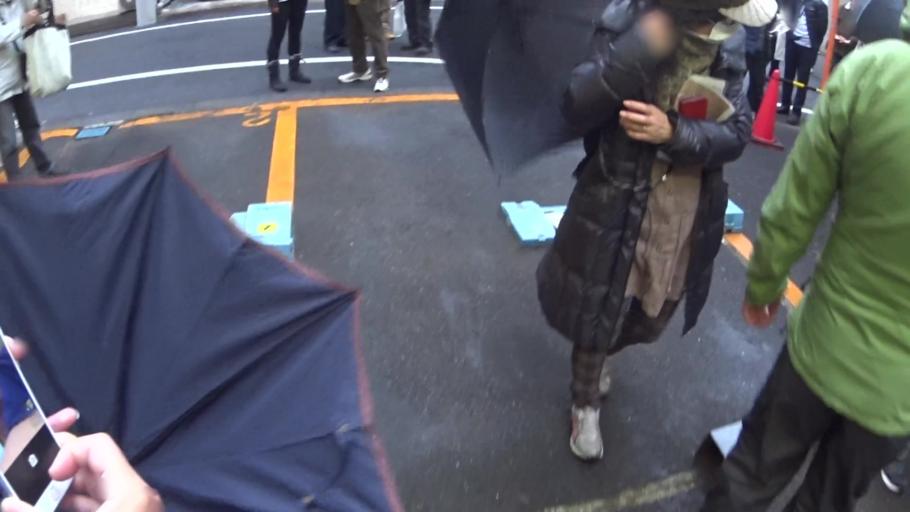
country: JP
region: Tokyo
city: Tokyo
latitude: 35.6925
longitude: 139.7233
